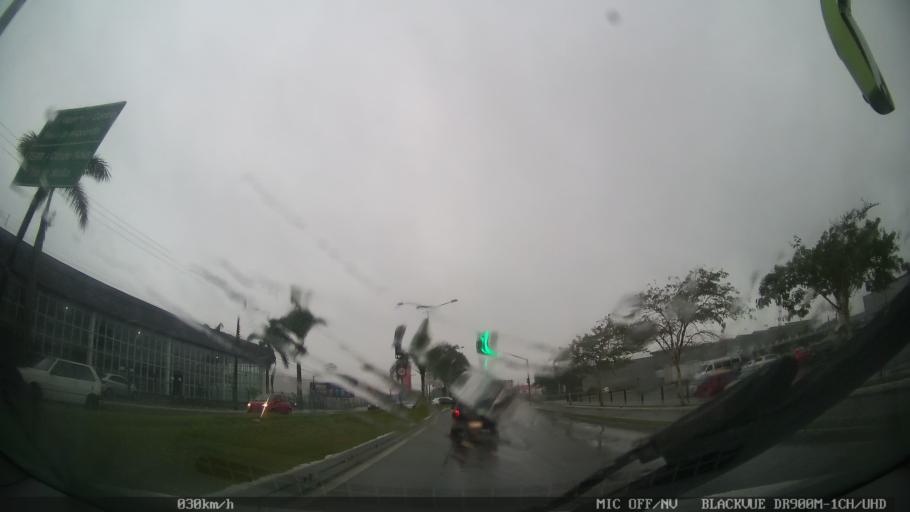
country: BR
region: Santa Catarina
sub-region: Itajai
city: Itajai
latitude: -26.9137
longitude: -48.6943
